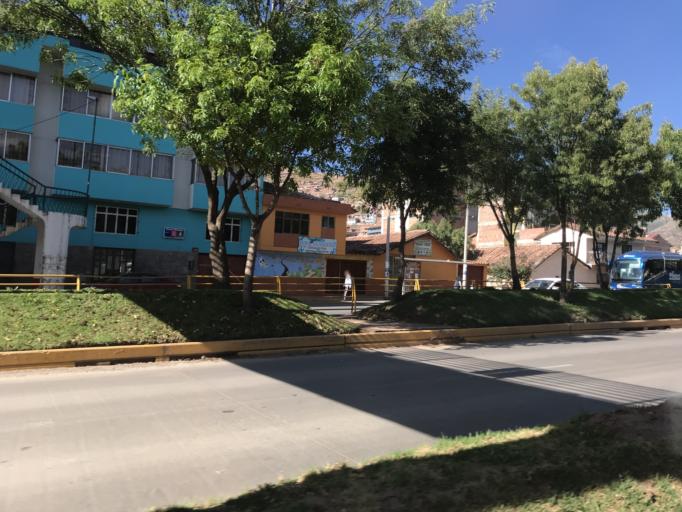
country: PE
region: Cusco
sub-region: Provincia de Cusco
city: Cusco
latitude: -13.5321
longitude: -71.9652
